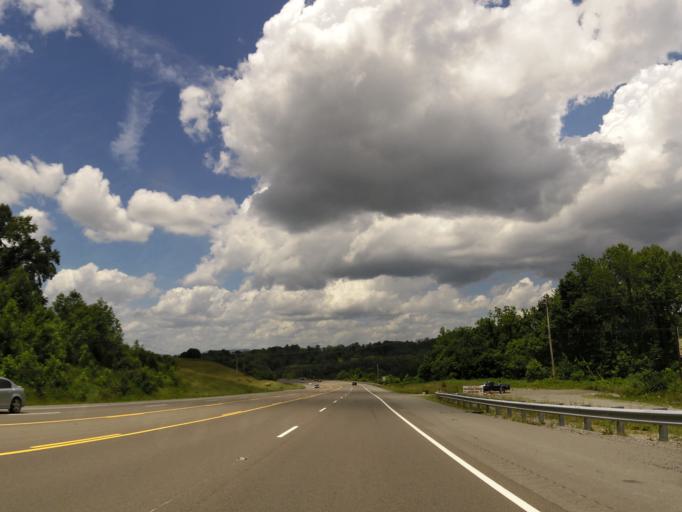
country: US
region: Tennessee
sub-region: Claiborne County
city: Tazewell
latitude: 36.4987
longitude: -83.5935
